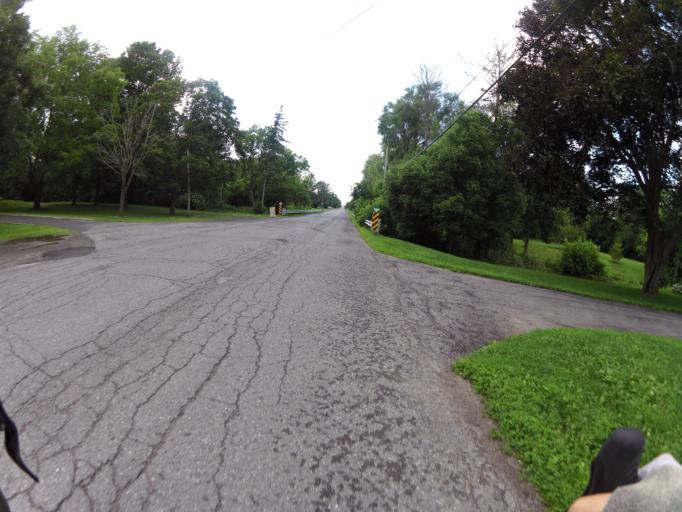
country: CA
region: Ontario
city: Bells Corners
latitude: 45.1873
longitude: -75.8351
